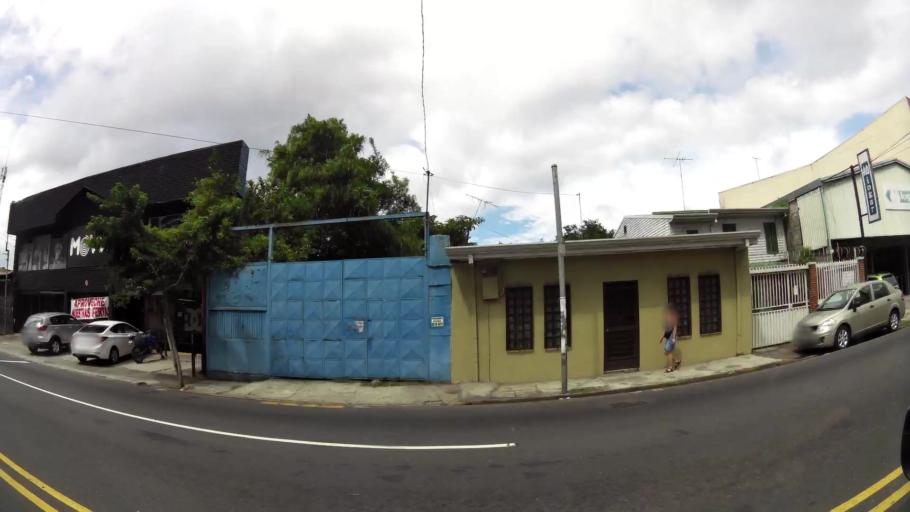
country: CR
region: San Jose
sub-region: Canton de Goicoechea
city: Guadalupe
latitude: 9.9445
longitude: -84.0576
